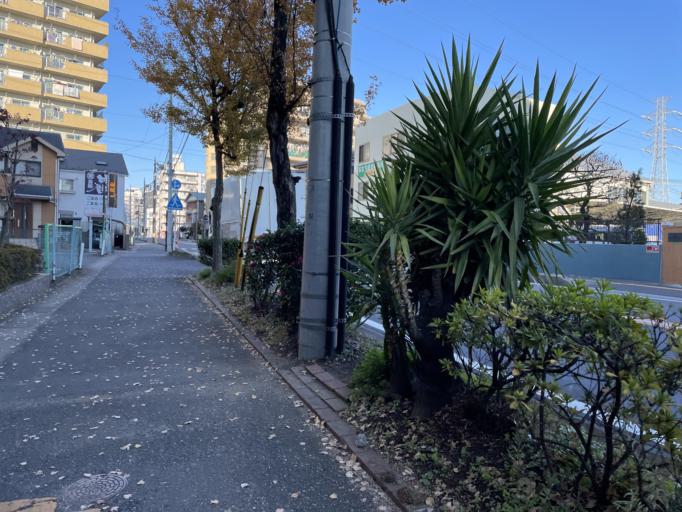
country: JP
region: Saitama
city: Soka
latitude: 35.8238
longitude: 139.8065
